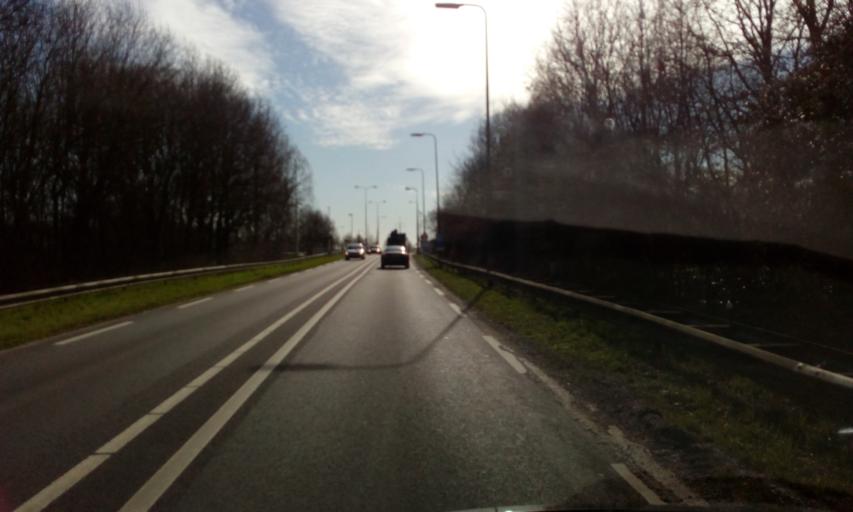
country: NL
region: South Holland
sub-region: Gemeente Alphen aan den Rijn
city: Alphen aan den Rijn
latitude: 52.1440
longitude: 4.7008
